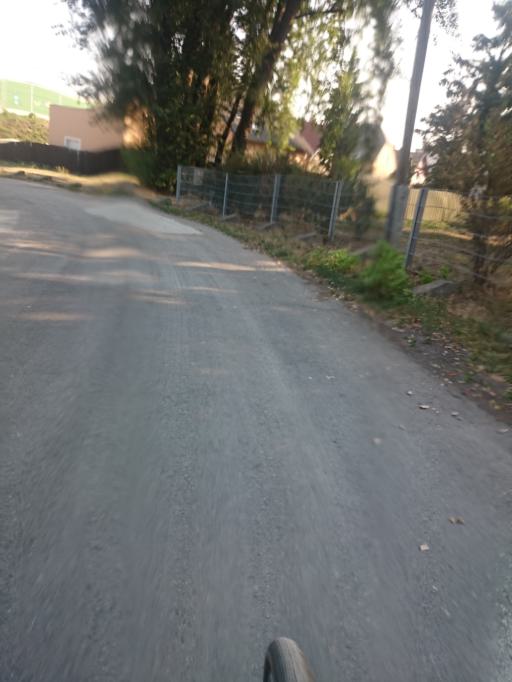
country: AT
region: Vienna
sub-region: Wien Stadt
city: Vienna
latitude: 48.2574
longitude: 16.3881
